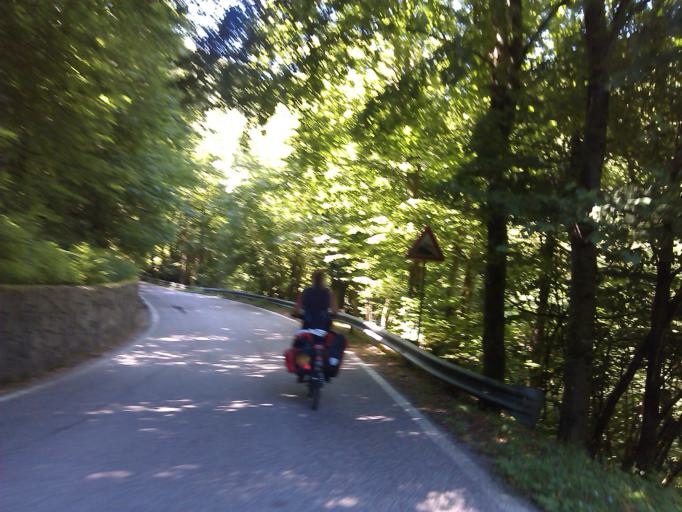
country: IT
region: Tuscany
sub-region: Provincia di Prato
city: Cantagallo
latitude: 44.0406
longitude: 11.0373
